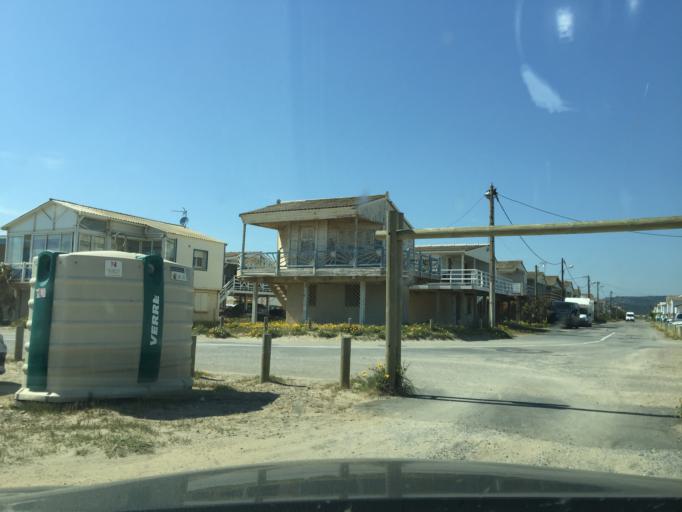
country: FR
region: Languedoc-Roussillon
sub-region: Departement de l'Aude
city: Gruissan
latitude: 43.1013
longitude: 3.1146
